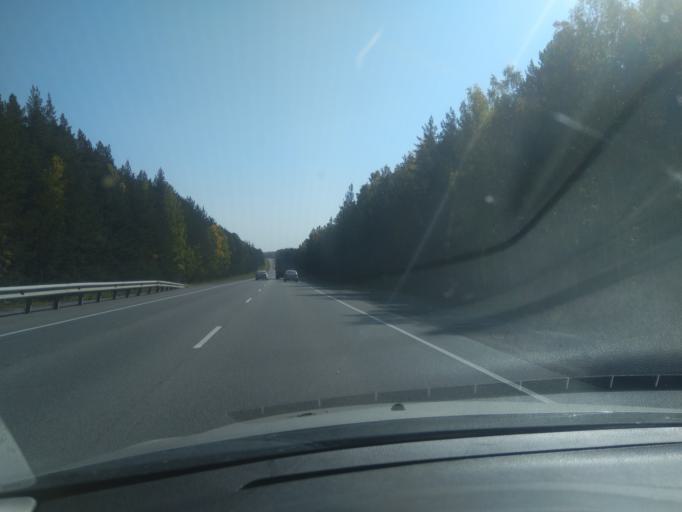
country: RU
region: Sverdlovsk
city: Dvurechensk
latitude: 56.6880
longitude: 61.1112
